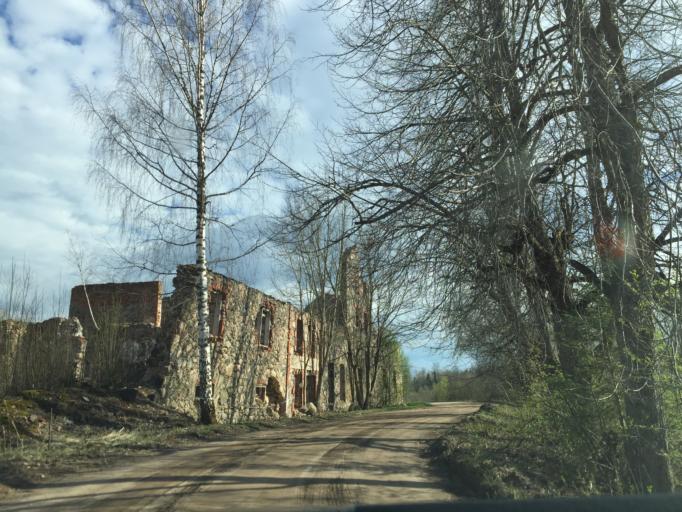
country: LV
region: Aluksnes Rajons
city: Aluksne
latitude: 57.4155
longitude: 26.9687
